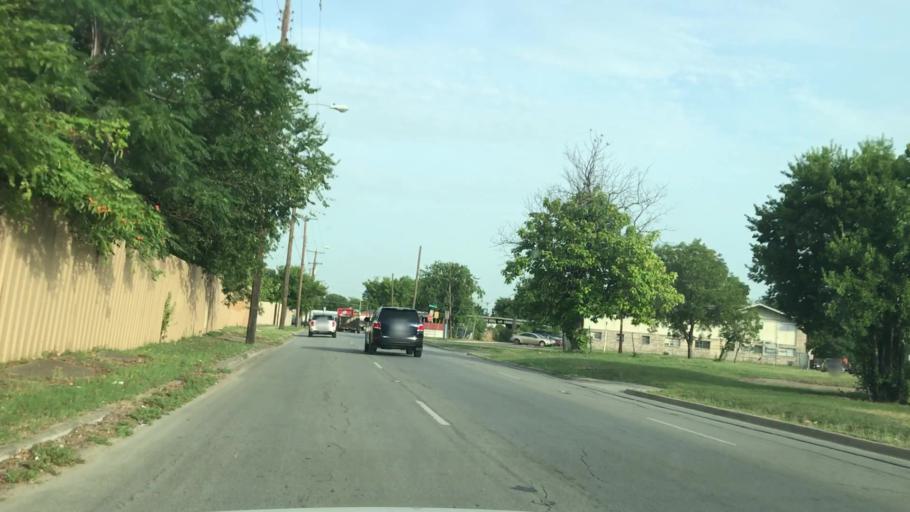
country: US
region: Texas
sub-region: Dallas County
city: Dallas
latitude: 32.7846
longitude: -96.7613
